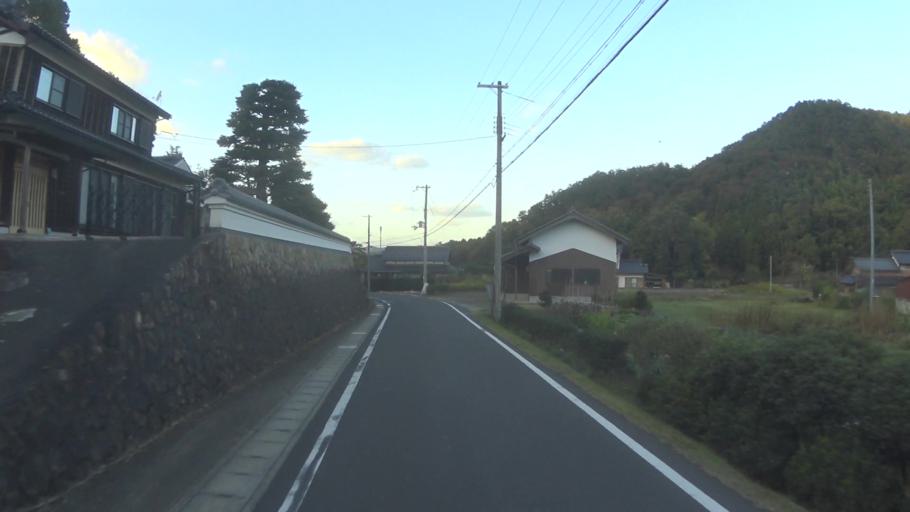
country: JP
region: Kyoto
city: Ayabe
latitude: 35.2900
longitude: 135.2379
